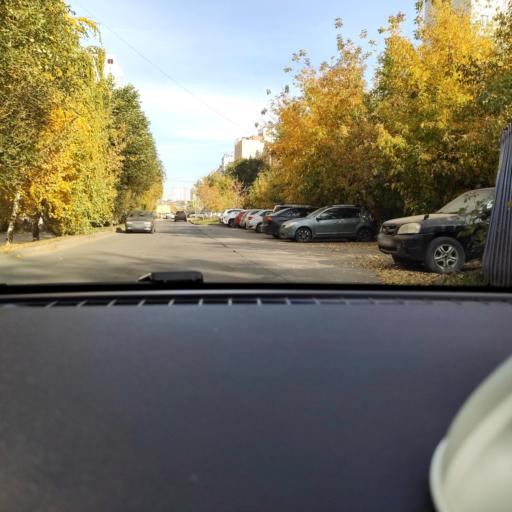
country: RU
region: Samara
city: Samara
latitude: 53.2148
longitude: 50.1642
